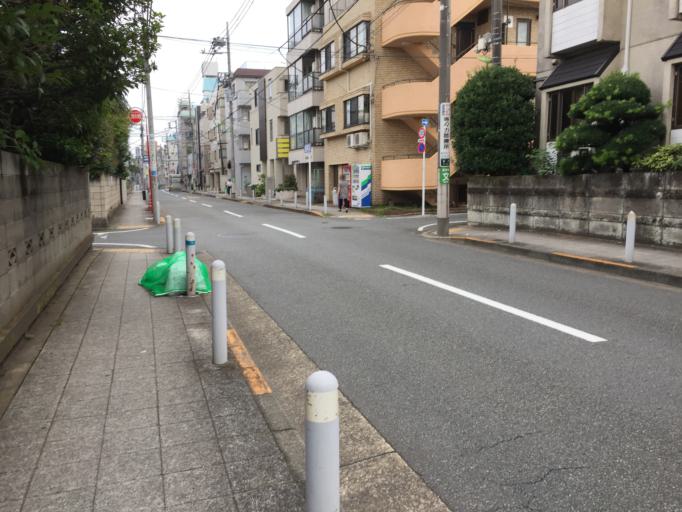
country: JP
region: Tokyo
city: Tokyo
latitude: 35.6060
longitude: 139.6605
